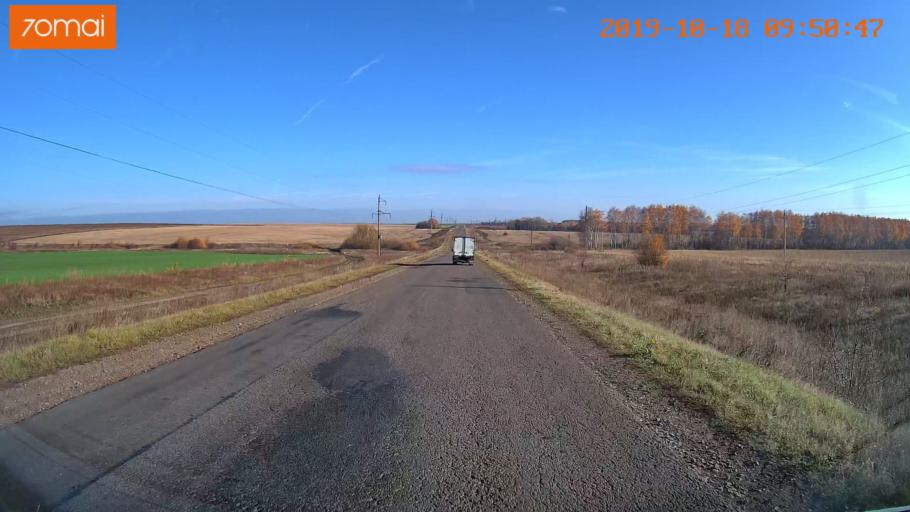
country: RU
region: Tula
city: Kazachka
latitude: 53.3327
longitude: 38.2823
